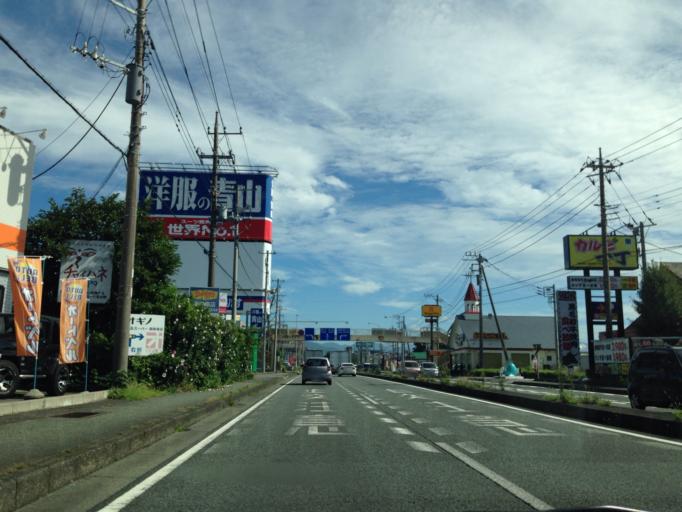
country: JP
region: Shizuoka
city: Gotemba
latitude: 35.3063
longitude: 138.9244
